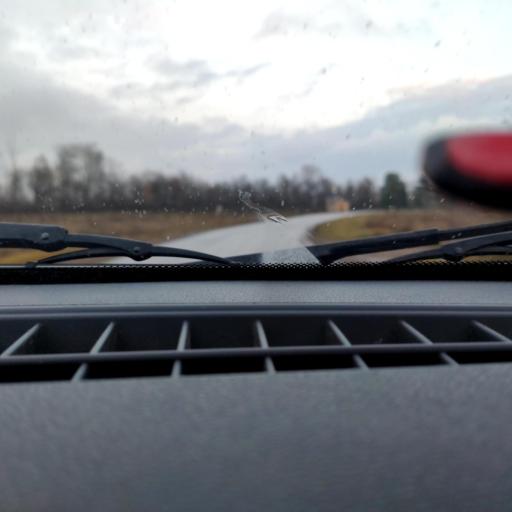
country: RU
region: Bashkortostan
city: Avdon
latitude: 54.5119
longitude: 55.8219
